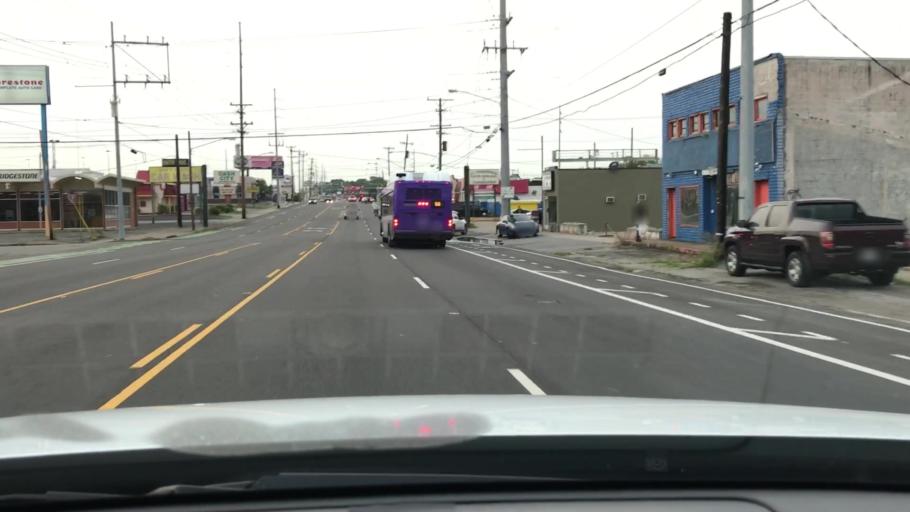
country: US
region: Tennessee
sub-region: Davidson County
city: Goodlettsville
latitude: 36.2594
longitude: -86.7132
